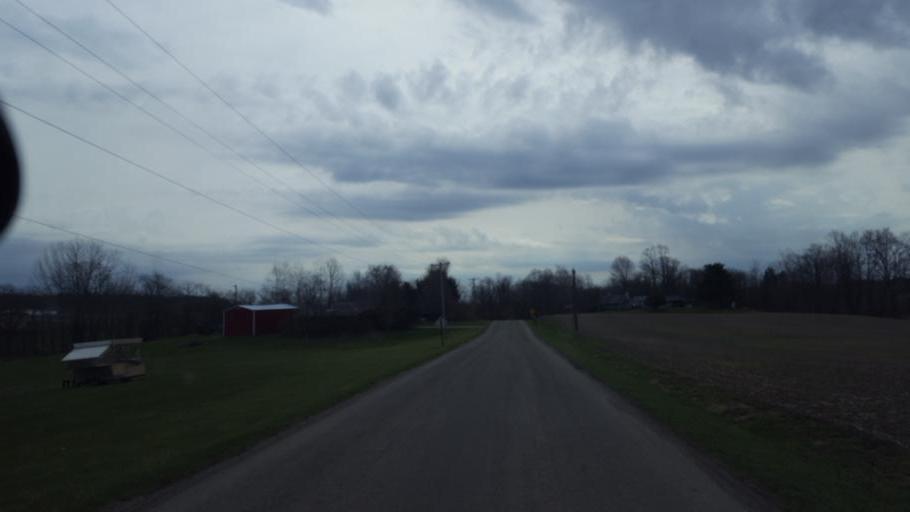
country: US
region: Ohio
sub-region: Morrow County
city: Mount Gilead
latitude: 40.5646
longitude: -82.6966
